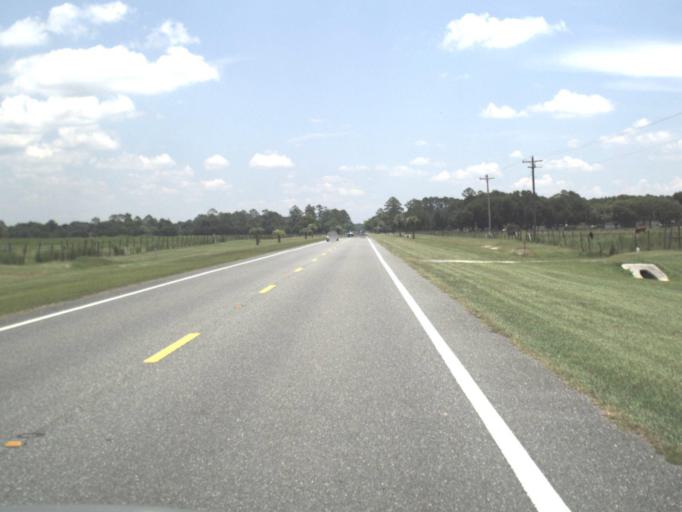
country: US
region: Florida
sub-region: Union County
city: Lake Butler
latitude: 30.0701
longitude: -82.2123
